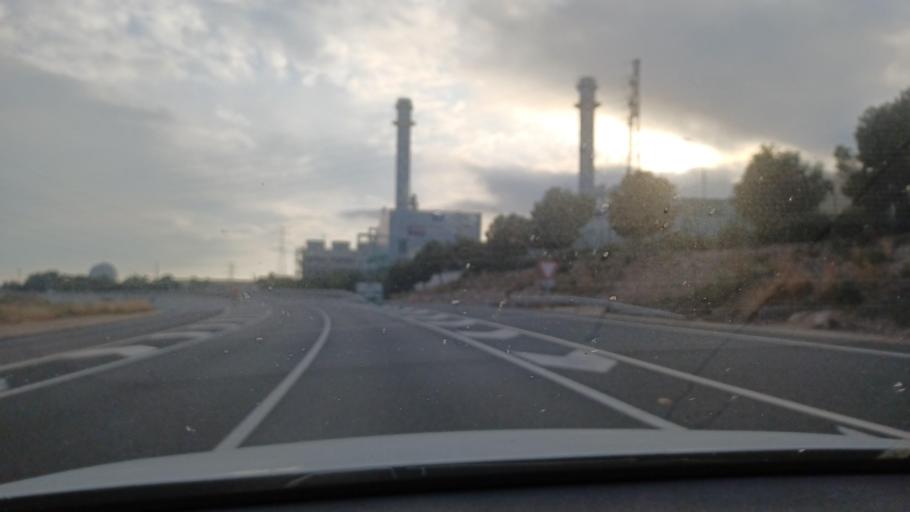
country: ES
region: Catalonia
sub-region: Provincia de Tarragona
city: l'Ametlla de Mar
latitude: 40.9607
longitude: 0.8721
